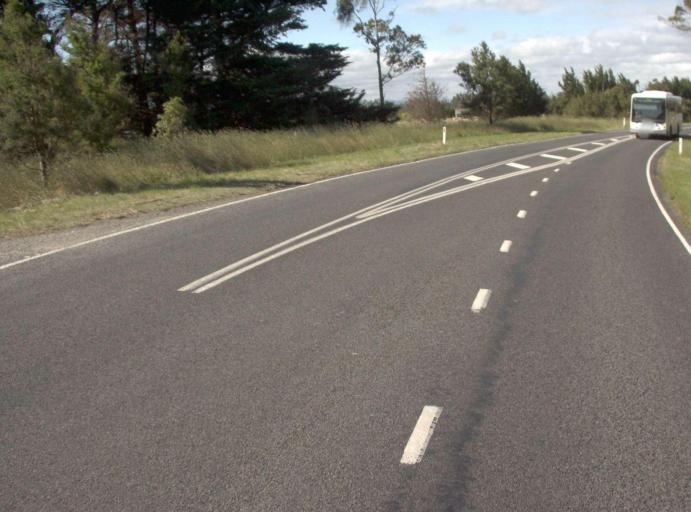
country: AU
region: Victoria
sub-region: Latrobe
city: Traralgon
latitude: -38.1628
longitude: 146.4916
